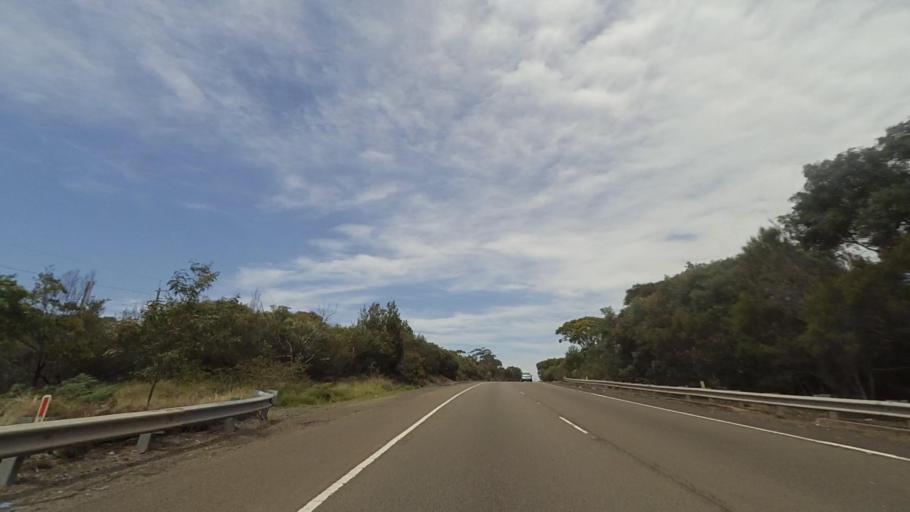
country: AU
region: New South Wales
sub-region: Sutherland Shire
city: Heathcote
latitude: -34.1100
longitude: 150.9934
